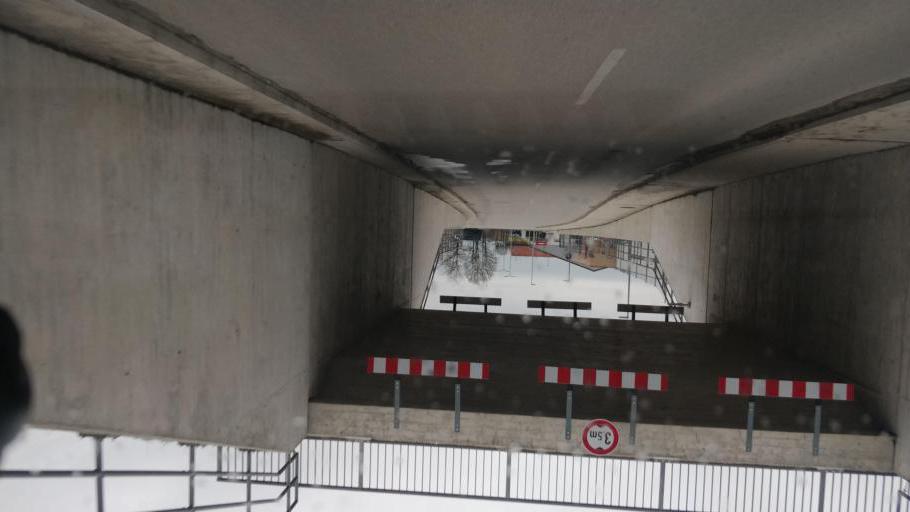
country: DE
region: Bavaria
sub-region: Upper Bavaria
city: Schwindegg
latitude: 48.2731
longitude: 12.2589
